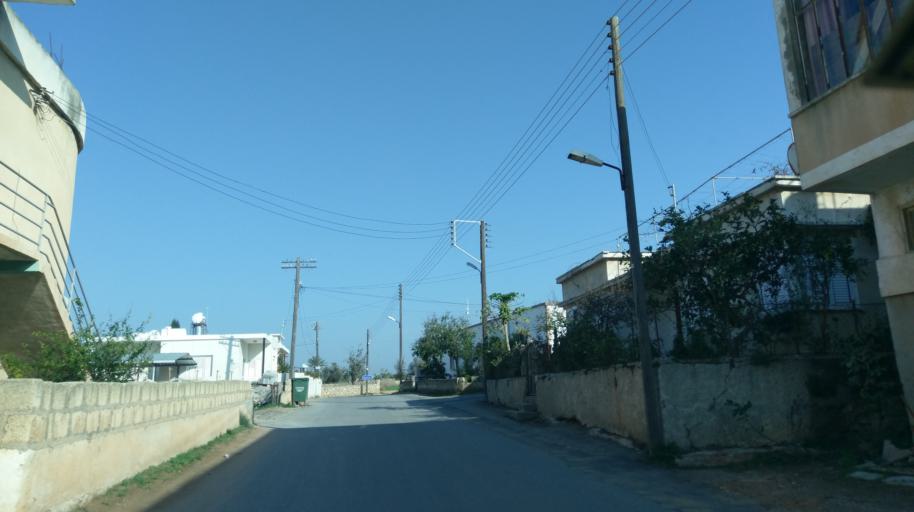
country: CY
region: Ammochostos
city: Leonarisso
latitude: 35.5336
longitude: 34.1893
